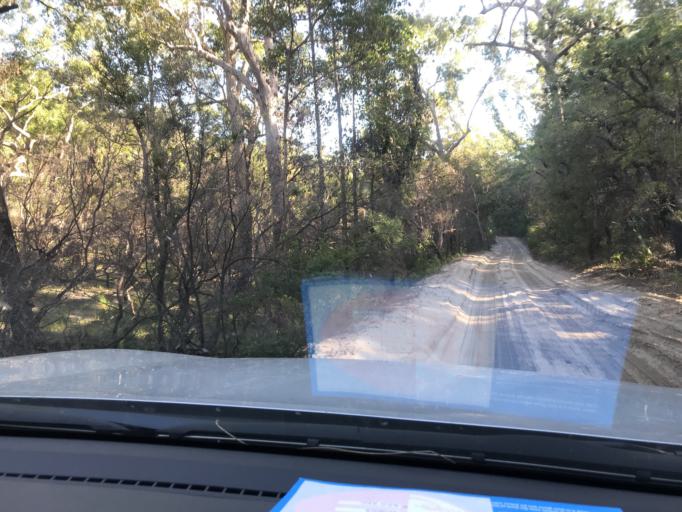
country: AU
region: Queensland
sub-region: Fraser Coast
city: Urangan
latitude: -25.5021
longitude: 153.1067
